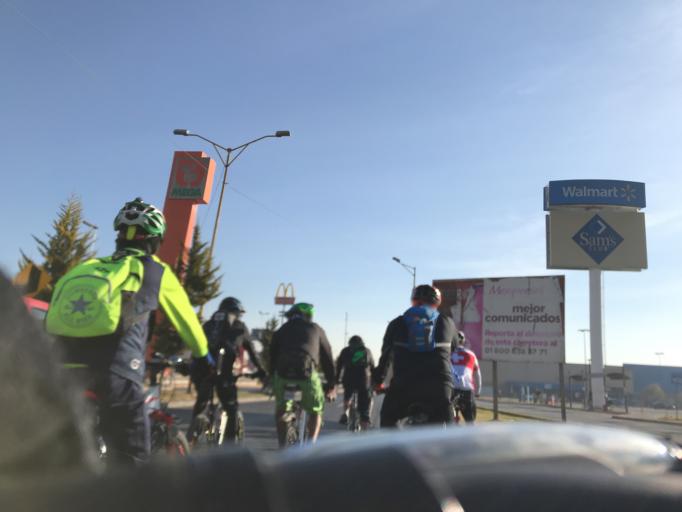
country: MX
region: Mexico
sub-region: Cuautitlan
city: La Trinidad
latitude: 19.6774
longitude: -99.1506
